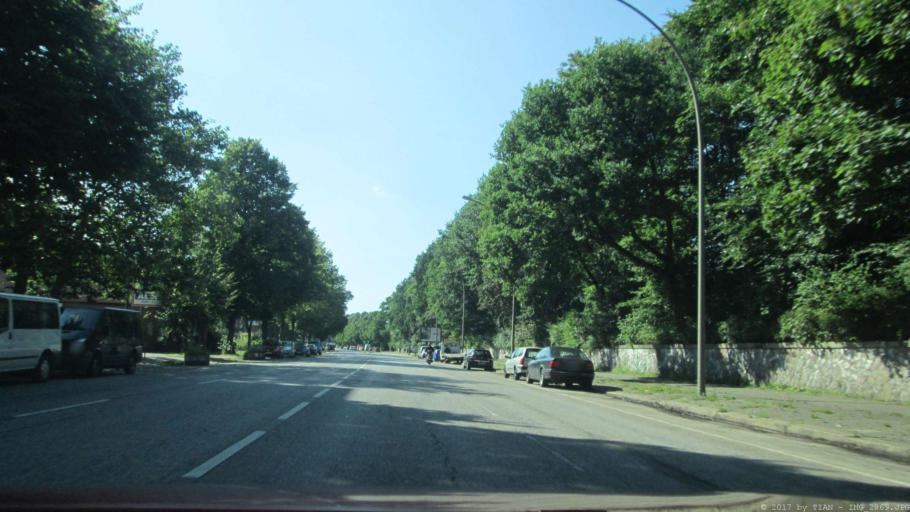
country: DE
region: Hamburg
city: Marienthal
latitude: 53.5513
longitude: 10.0754
